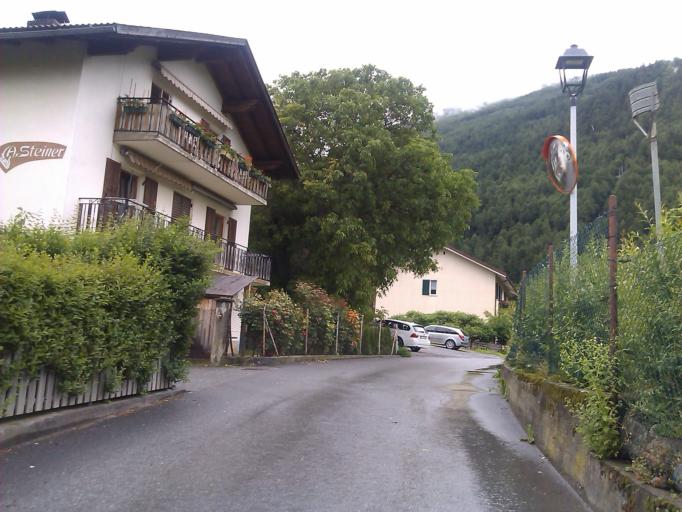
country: IT
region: Trentino-Alto Adige
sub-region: Bolzano
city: Lasa
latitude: 46.6131
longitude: 10.7062
